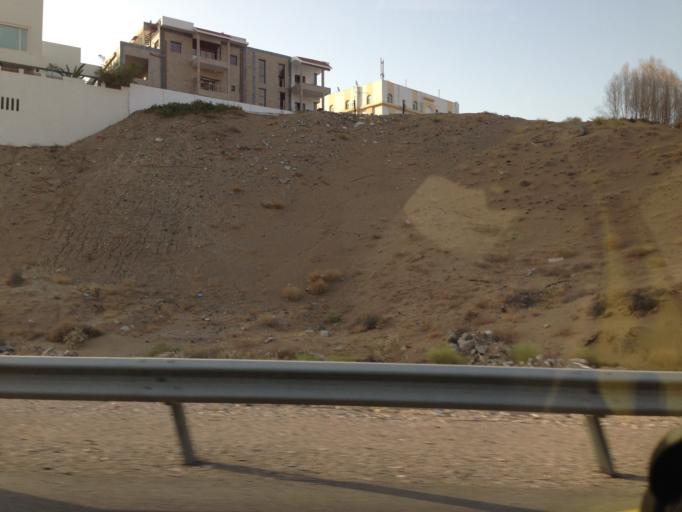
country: OM
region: Muhafazat Masqat
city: Bawshar
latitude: 23.5764
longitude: 58.4357
